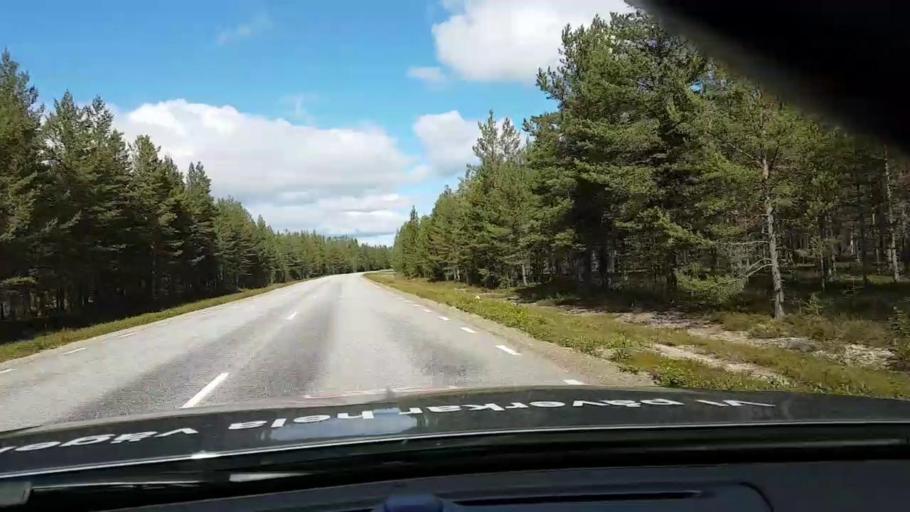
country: SE
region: Vaesternorrland
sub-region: OErnskoeldsviks Kommun
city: Bredbyn
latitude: 63.6202
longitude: 17.9070
